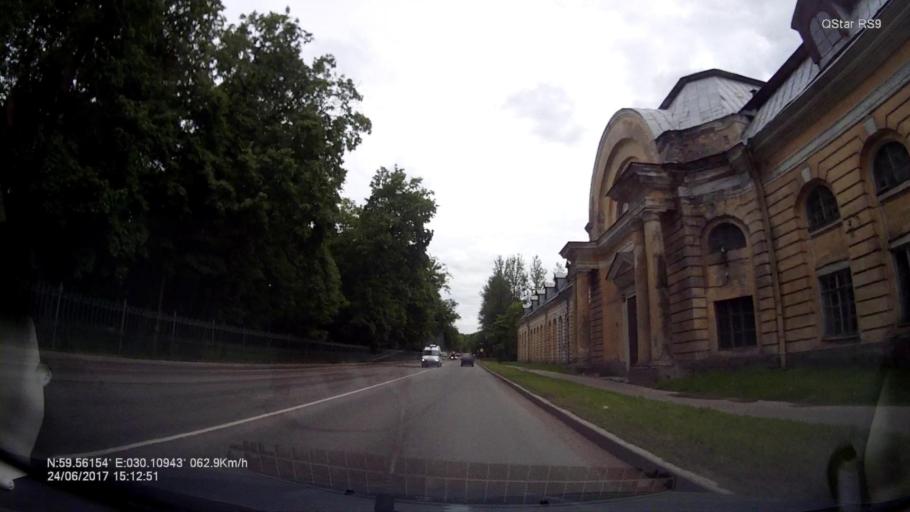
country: RU
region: Leningrad
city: Gatchina
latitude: 59.5614
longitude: 30.1097
